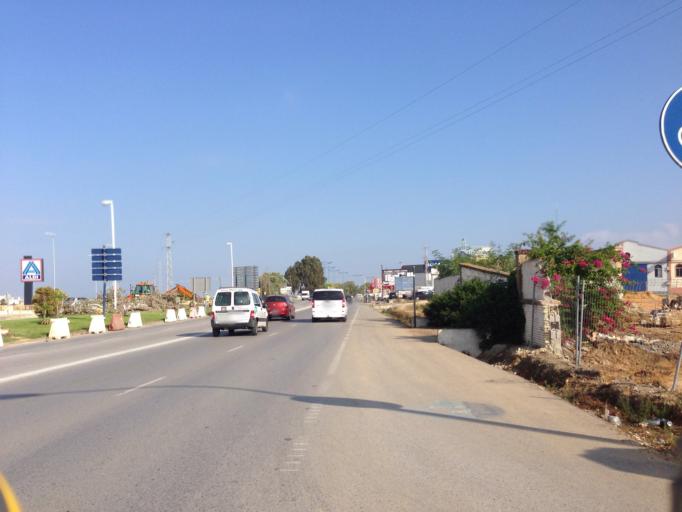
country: ES
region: Andalusia
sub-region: Provincia de Cadiz
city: Chiclana de la Frontera
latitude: 36.4306
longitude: -6.1430
